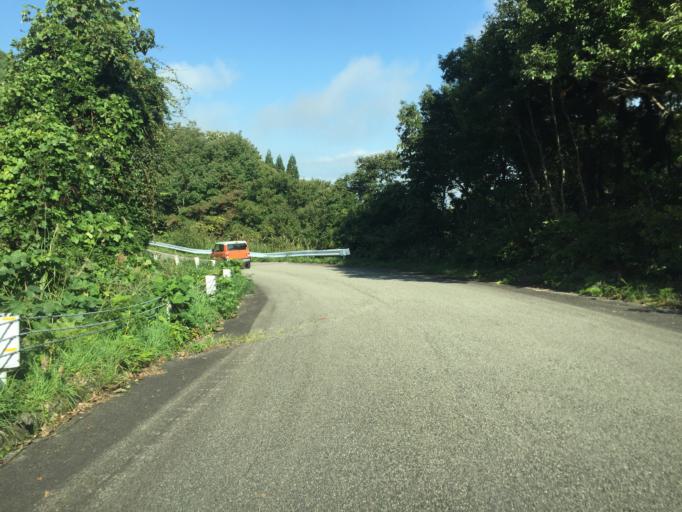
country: JP
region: Fukushima
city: Inawashiro
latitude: 37.4840
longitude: 139.9741
